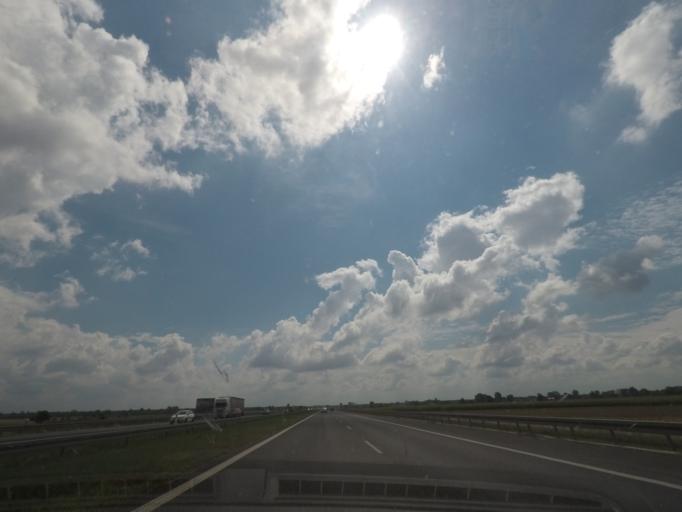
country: PL
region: Lodz Voivodeship
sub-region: Powiat zgierski
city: Strykow
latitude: 51.9710
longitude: 19.5756
